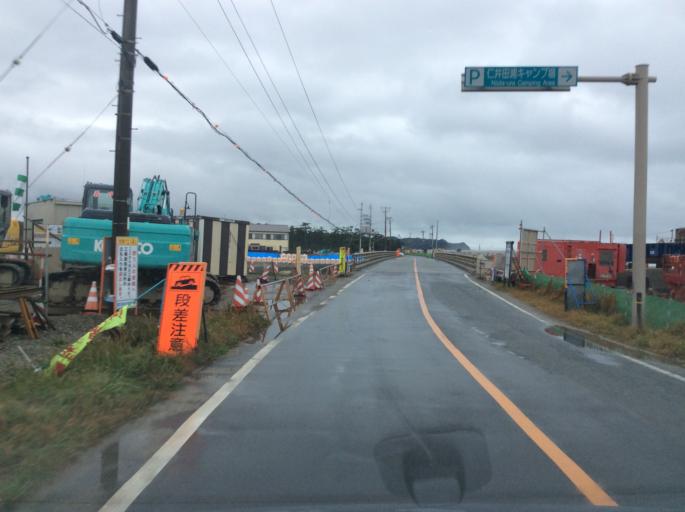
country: JP
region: Fukushima
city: Iwaki
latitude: 37.0893
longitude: 140.9820
